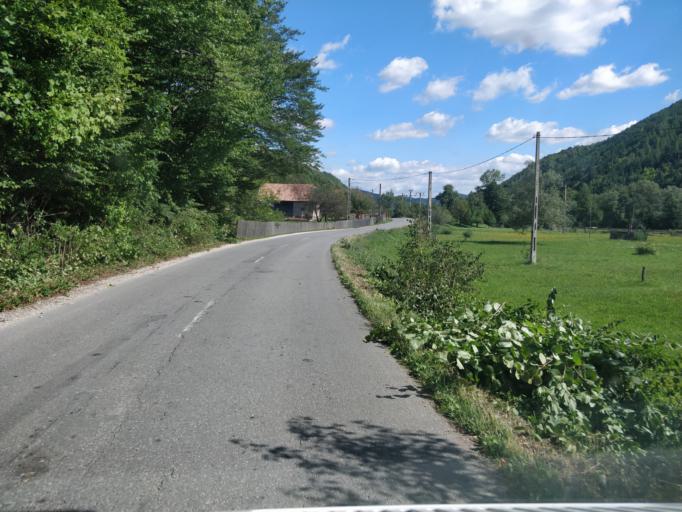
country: RO
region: Cluj
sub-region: Comuna Sacueu
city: Sacuieu
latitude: 46.8564
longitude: 22.8646
